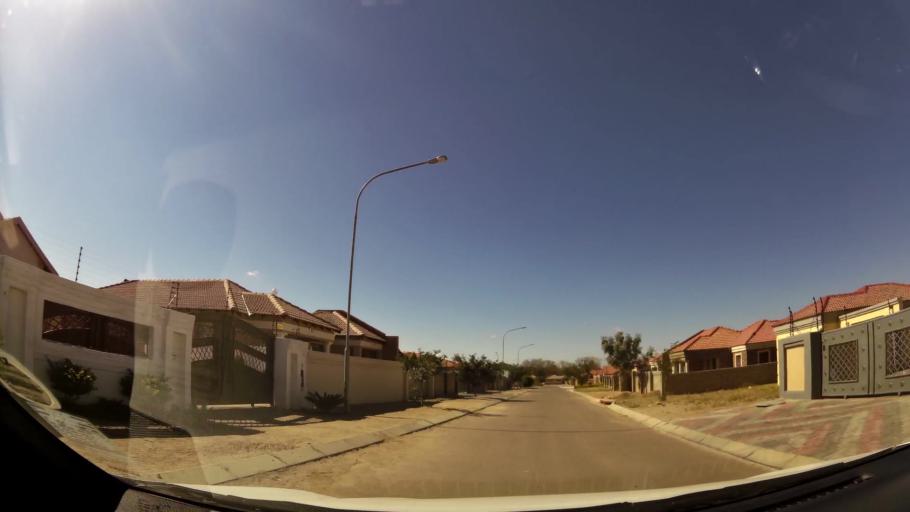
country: ZA
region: Limpopo
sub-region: Capricorn District Municipality
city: Polokwane
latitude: -23.8598
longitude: 29.4244
